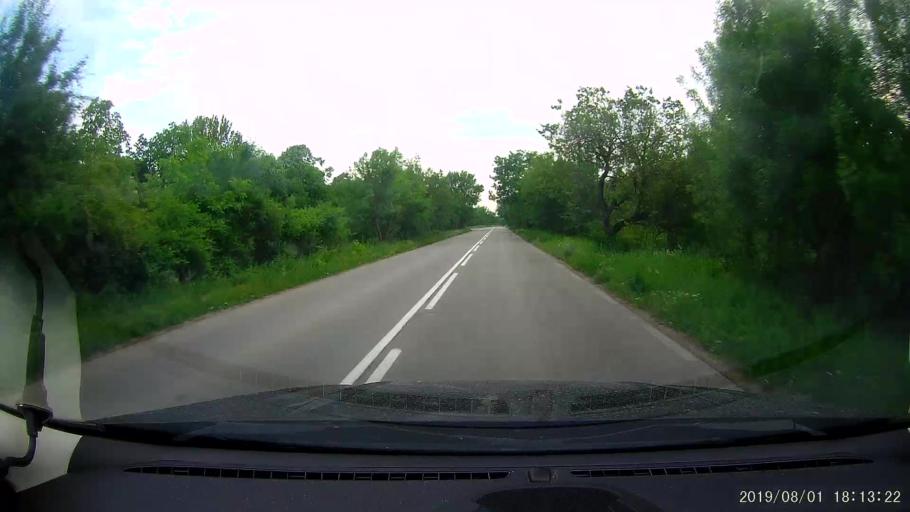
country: BG
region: Silistra
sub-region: Obshtina Dulovo
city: Dulovo
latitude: 43.7907
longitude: 27.1409
